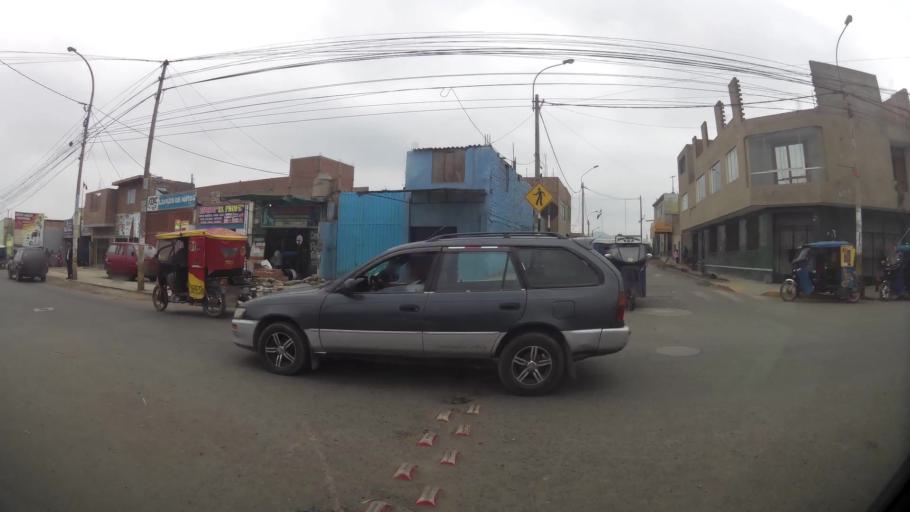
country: PE
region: Lima
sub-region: Provincia de Huaral
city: Huaral
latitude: -11.4935
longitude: -77.2003
